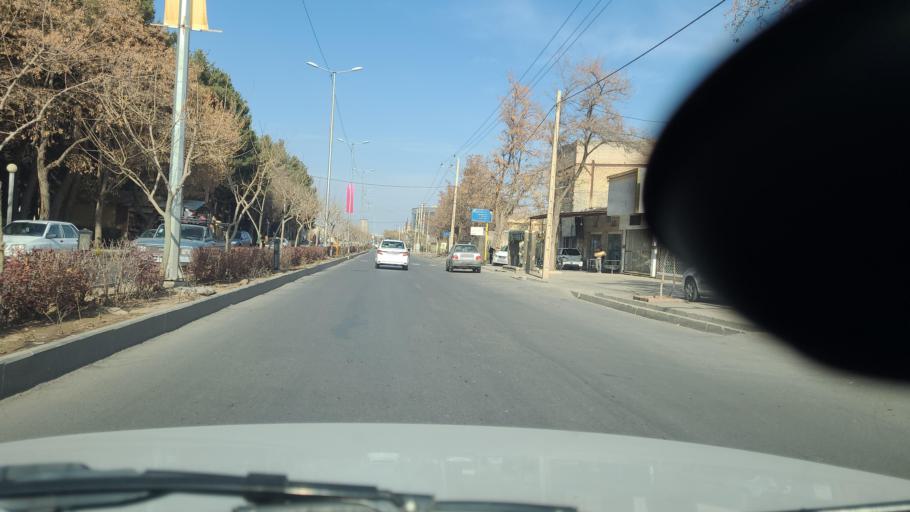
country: IR
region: Razavi Khorasan
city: Fariman
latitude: 35.6925
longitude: 59.8442
